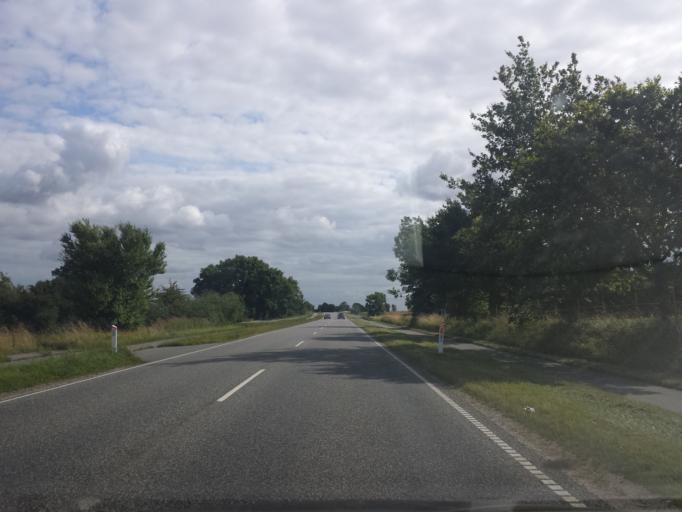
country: DK
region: South Denmark
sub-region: Sonderborg Kommune
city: Guderup
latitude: 55.0099
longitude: 9.8458
